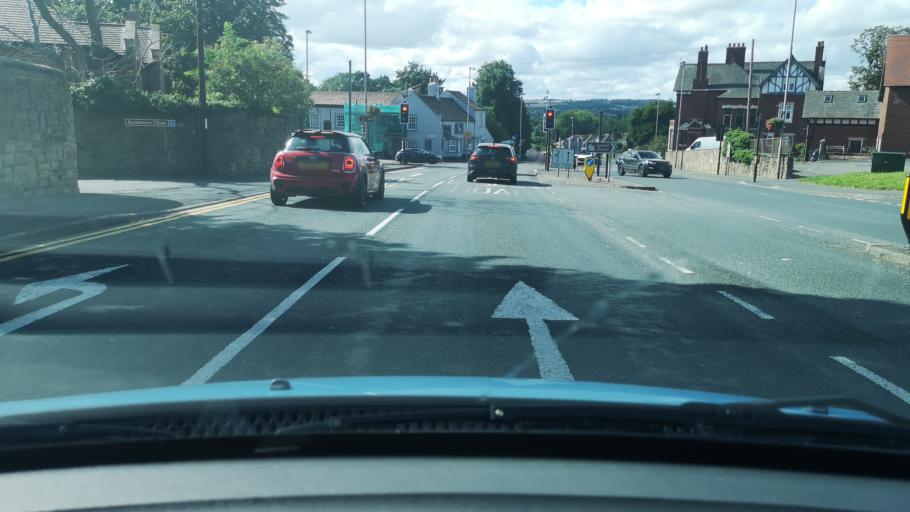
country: GB
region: England
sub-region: City and Borough of Wakefield
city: Walton
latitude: 53.6552
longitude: -1.4869
